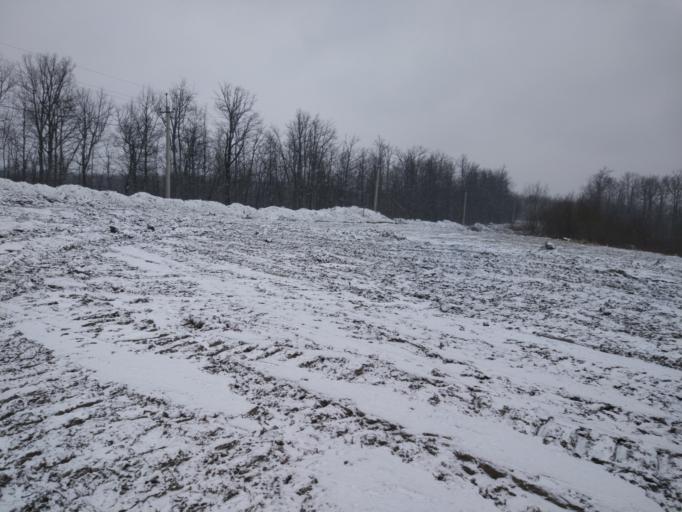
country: RU
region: Krasnodarskiy
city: Saratovskaya
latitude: 44.6175
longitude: 39.2359
